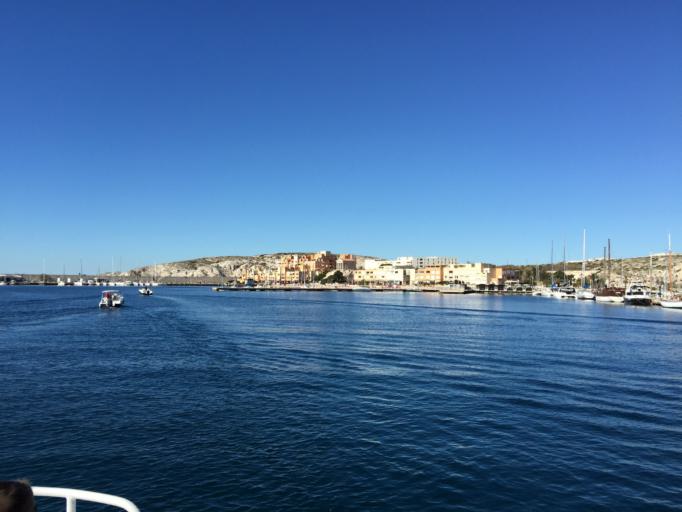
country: FR
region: Provence-Alpes-Cote d'Azur
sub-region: Departement des Bouches-du-Rhone
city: Marseille 07
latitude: 43.2777
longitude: 5.3089
